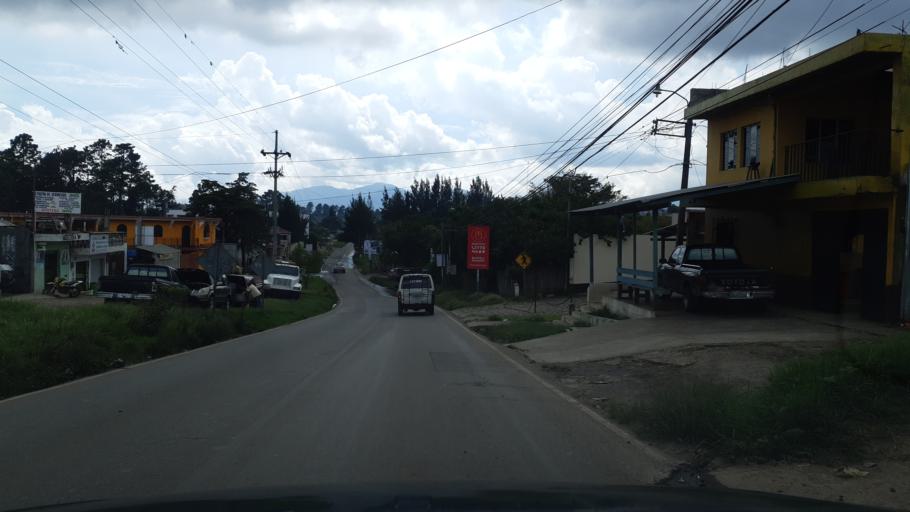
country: GT
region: Chimaltenango
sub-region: Municipio de Chimaltenango
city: Chimaltenango
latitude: 14.6807
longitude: -90.7990
